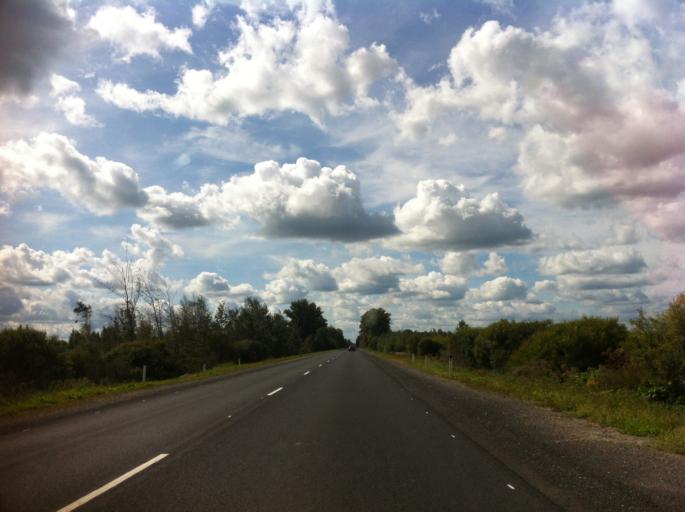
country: RU
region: Pskov
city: Izborsk
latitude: 57.7361
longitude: 27.9941
